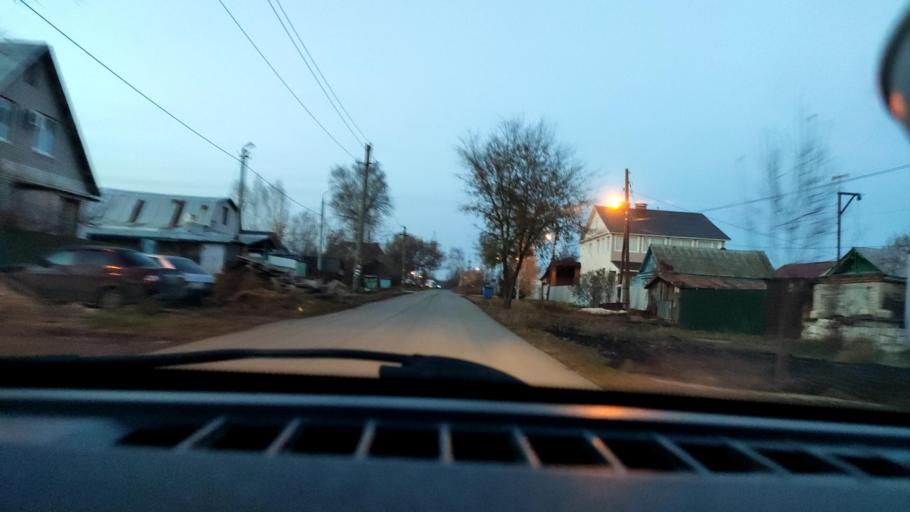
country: RU
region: Samara
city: Petra-Dubrava
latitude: 53.2606
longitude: 50.3297
